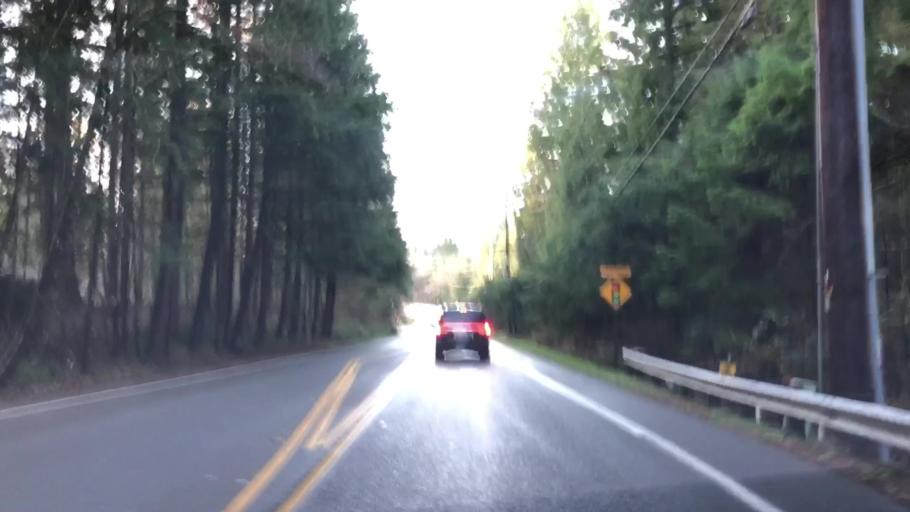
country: US
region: Washington
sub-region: King County
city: City of Sammamish
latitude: 47.5695
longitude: -122.0239
